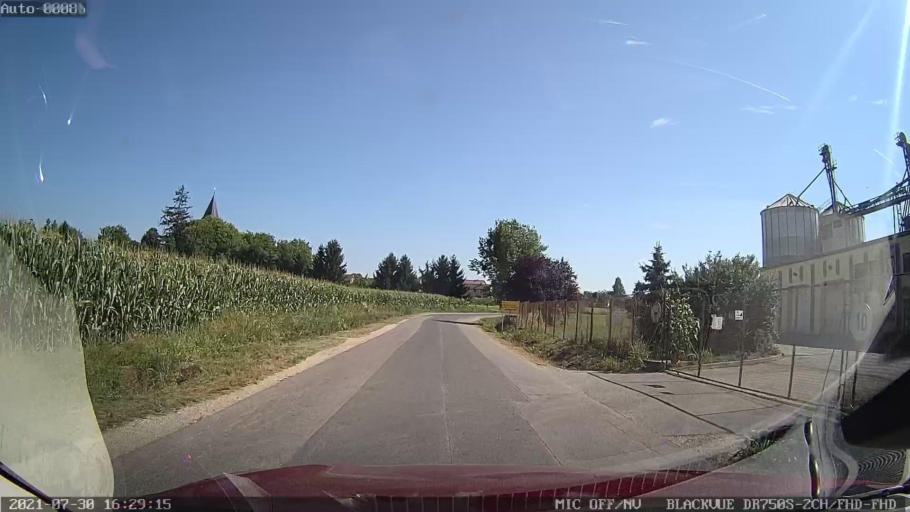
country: HR
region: Varazdinska
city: Jalzabet
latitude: 46.2590
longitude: 16.4337
